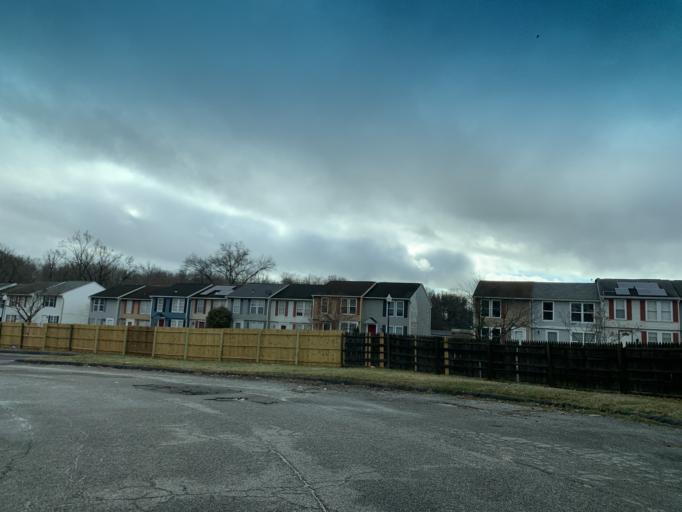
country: US
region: Maryland
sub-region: Harford County
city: Edgewood
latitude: 39.4244
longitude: -76.2976
